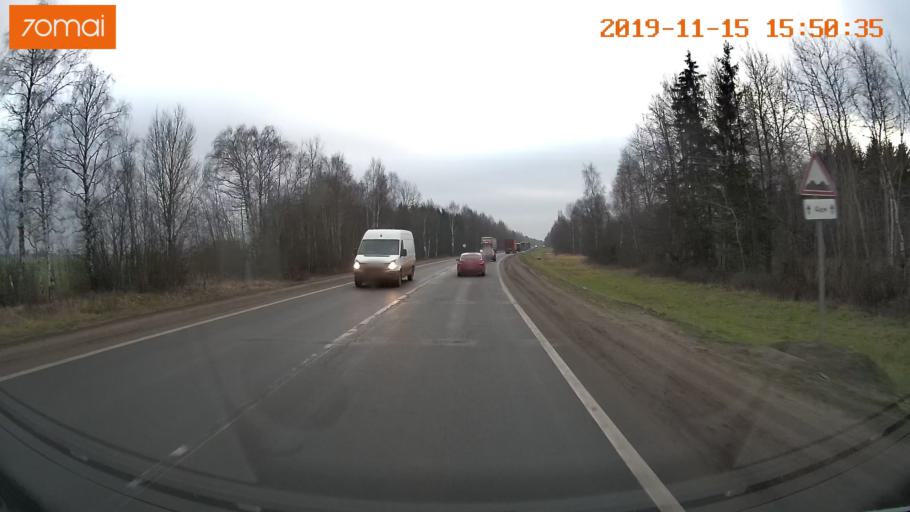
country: RU
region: Jaroslavl
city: Yaroslavl
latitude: 57.9041
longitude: 40.0134
